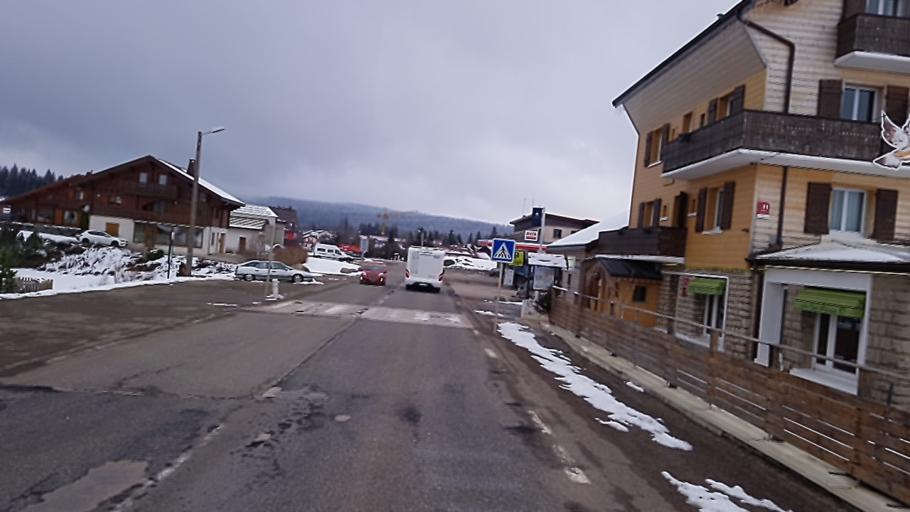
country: FR
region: Franche-Comte
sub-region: Departement du Jura
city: Les Rousses
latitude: 46.4766
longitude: 6.0651
